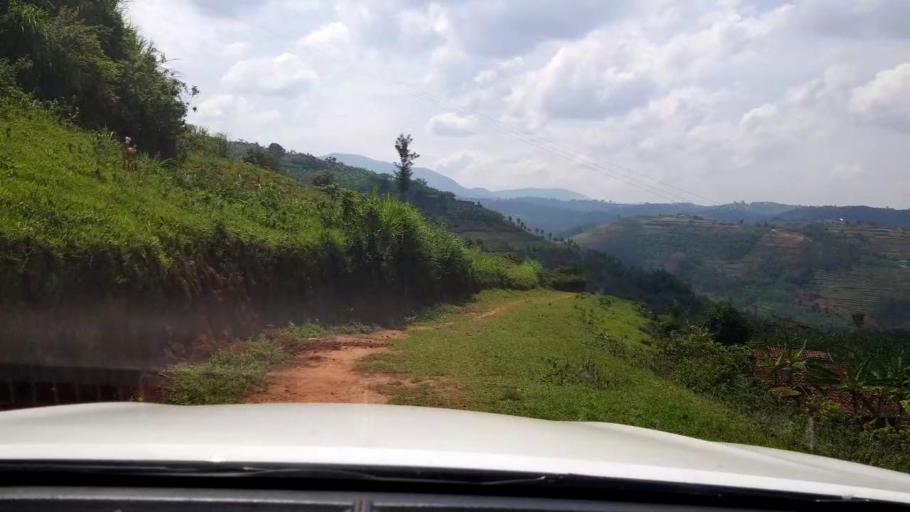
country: RW
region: Southern Province
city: Gitarama
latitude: -2.0583
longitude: 29.6670
